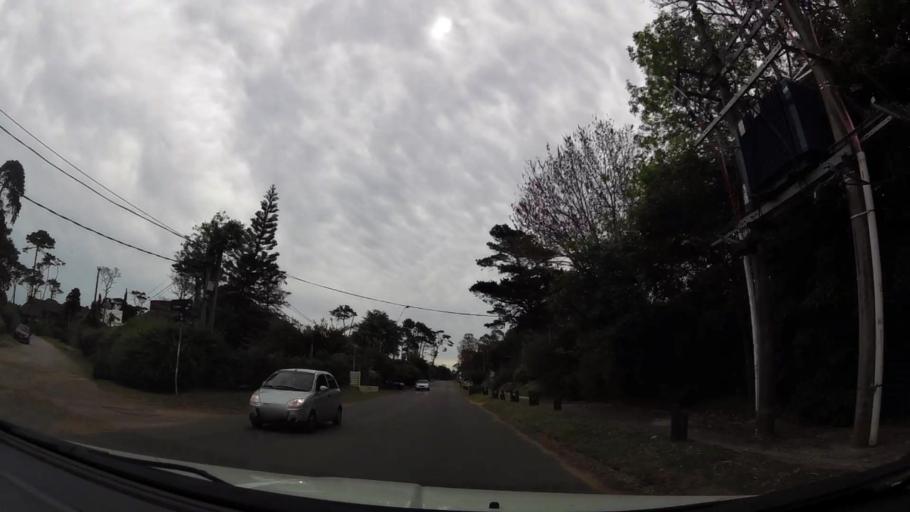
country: UY
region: Maldonado
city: Maldonado
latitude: -34.9091
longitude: -54.9872
